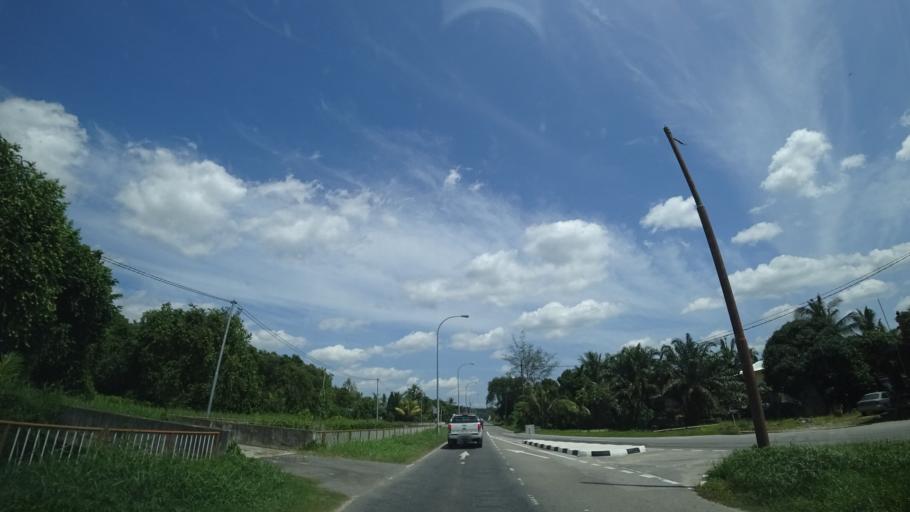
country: BN
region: Brunei and Muara
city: Bandar Seri Begawan
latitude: 4.8691
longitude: 114.8482
